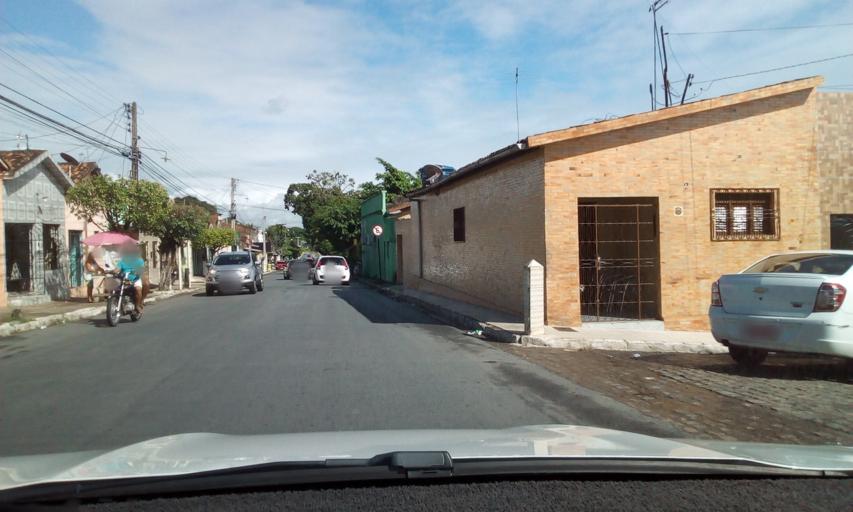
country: BR
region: Paraiba
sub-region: Santa Rita
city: Santa Rita
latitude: -7.1238
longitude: -34.9696
